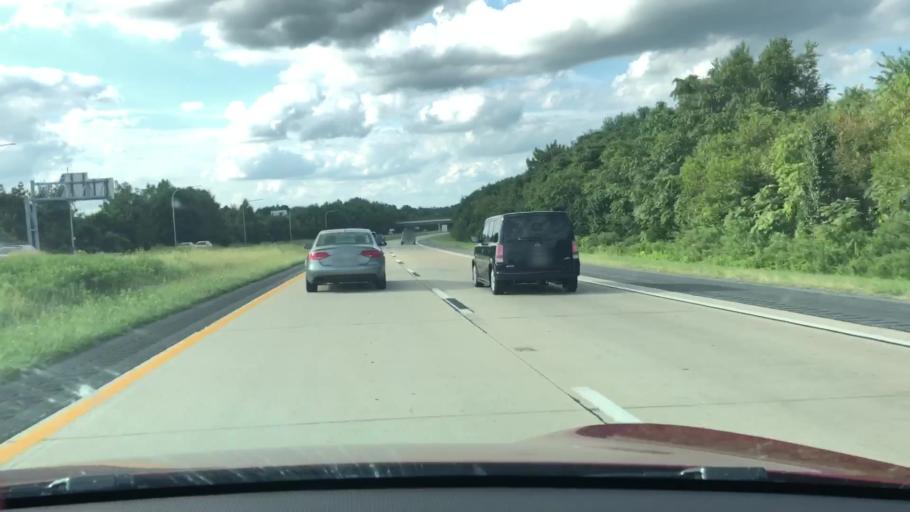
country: US
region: Delaware
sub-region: Kent County
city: Smyrna
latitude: 39.2870
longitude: -75.5920
